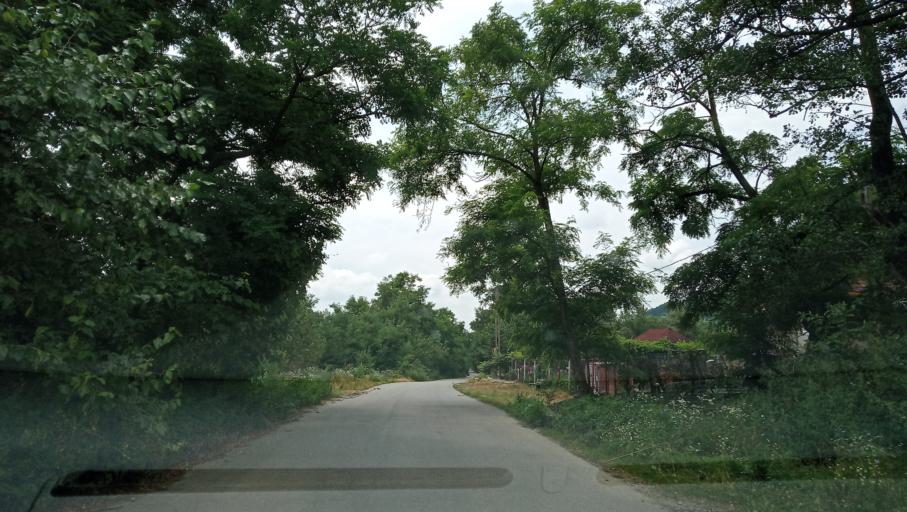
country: RO
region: Gorj
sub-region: Comuna Bumbesti-Jiu
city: Bumbesti-Jiu
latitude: 45.1585
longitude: 23.3508
